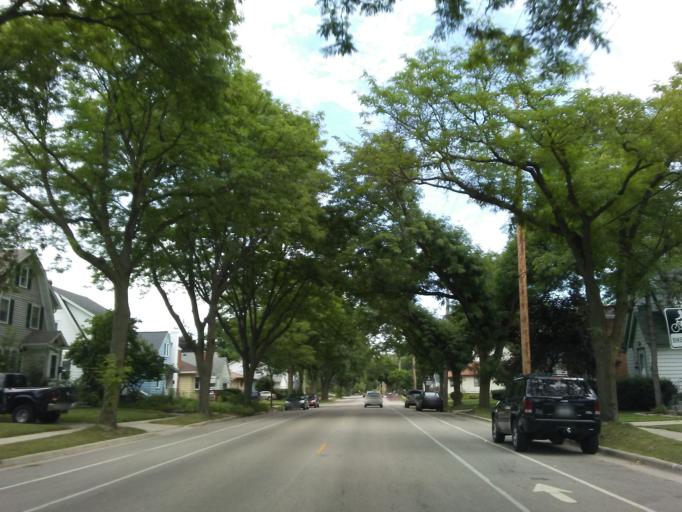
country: US
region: Wisconsin
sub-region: Dane County
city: Maple Bluff
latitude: 43.1068
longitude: -89.3452
